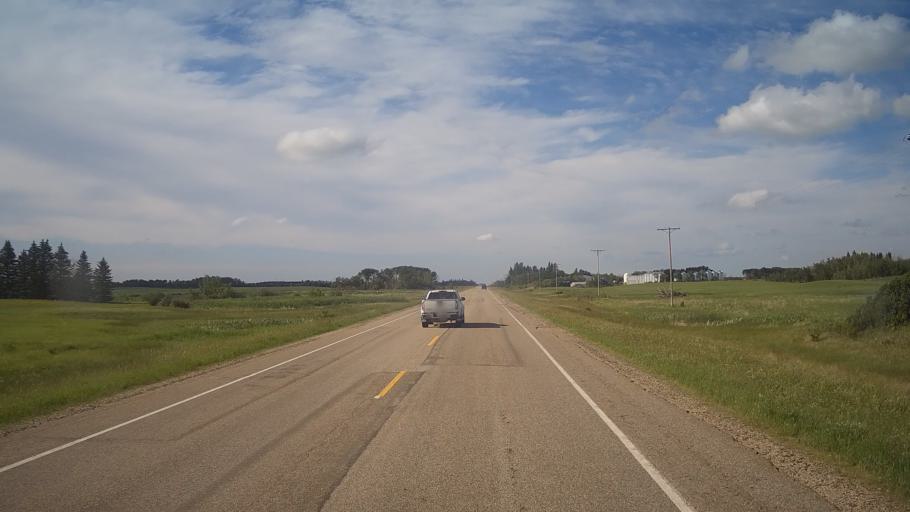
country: CA
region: Saskatchewan
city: Foam Lake
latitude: 51.5844
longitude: -103.8458
